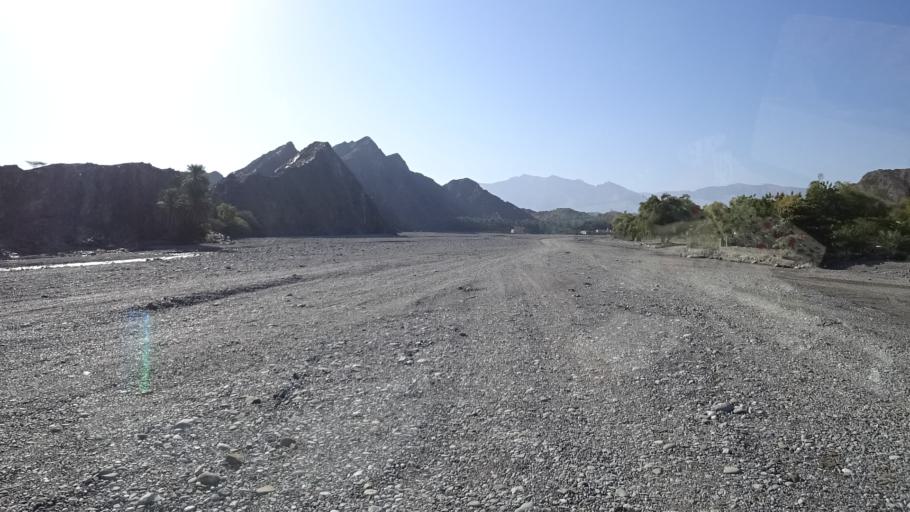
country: OM
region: Al Batinah
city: Bayt al `Awabi
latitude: 23.3959
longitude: 57.6629
